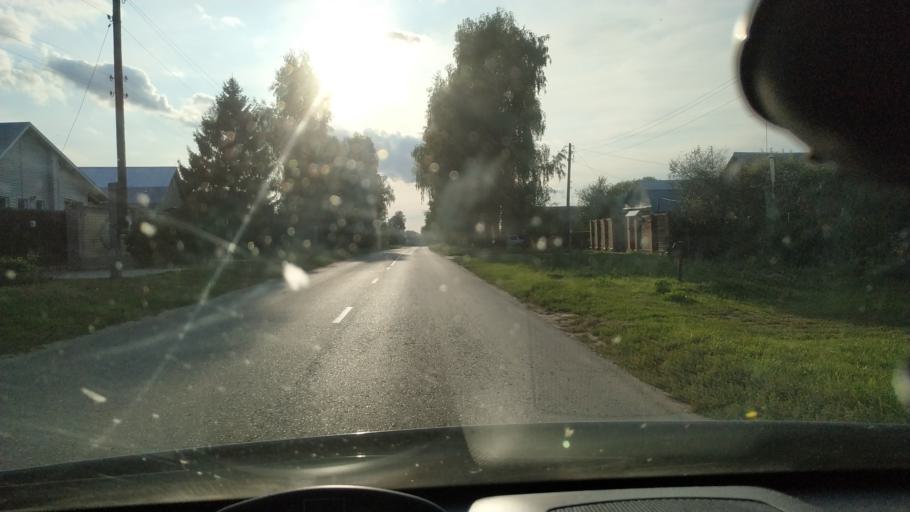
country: RU
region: Rjazan
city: Solotcha
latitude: 54.8665
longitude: 39.6616
